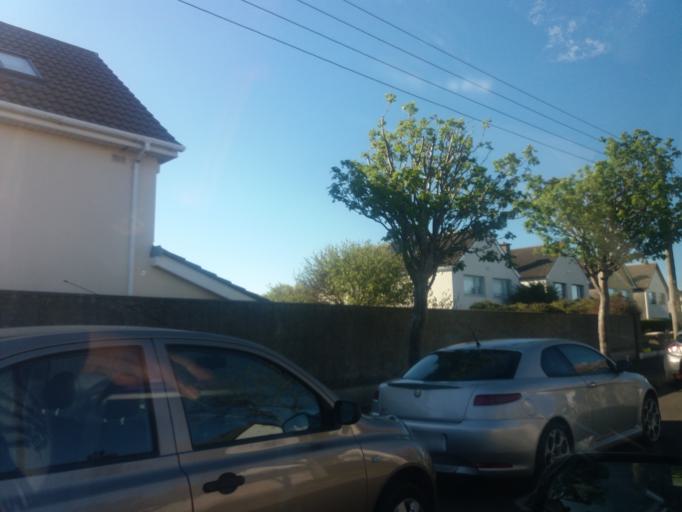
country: IE
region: Leinster
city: Sutton
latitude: 53.3777
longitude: -6.0999
